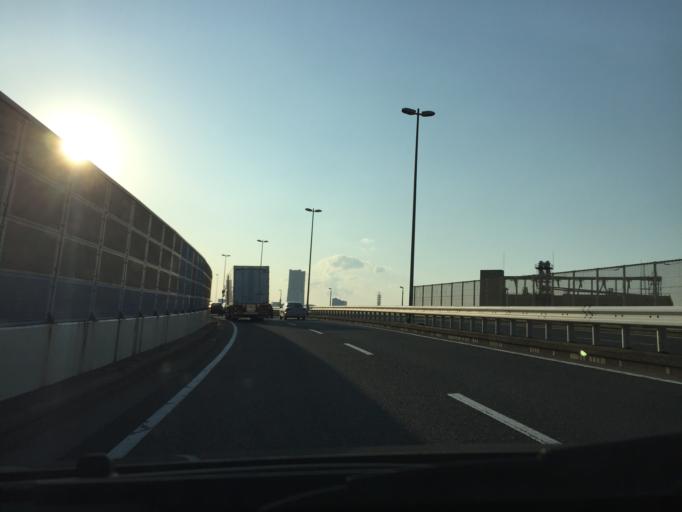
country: JP
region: Kanagawa
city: Yokohama
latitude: 35.4428
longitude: 139.6576
